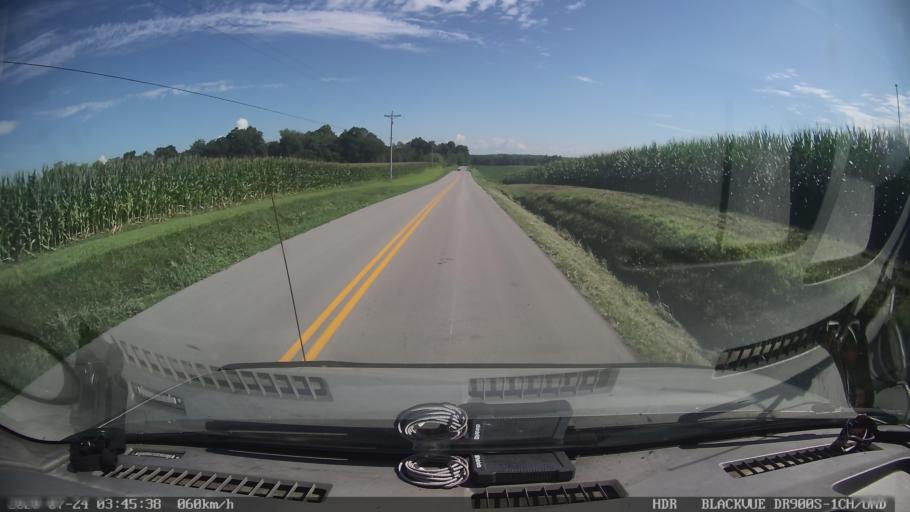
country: US
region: Kentucky
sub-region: Todd County
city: Elkton
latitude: 36.7476
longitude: -87.2254
